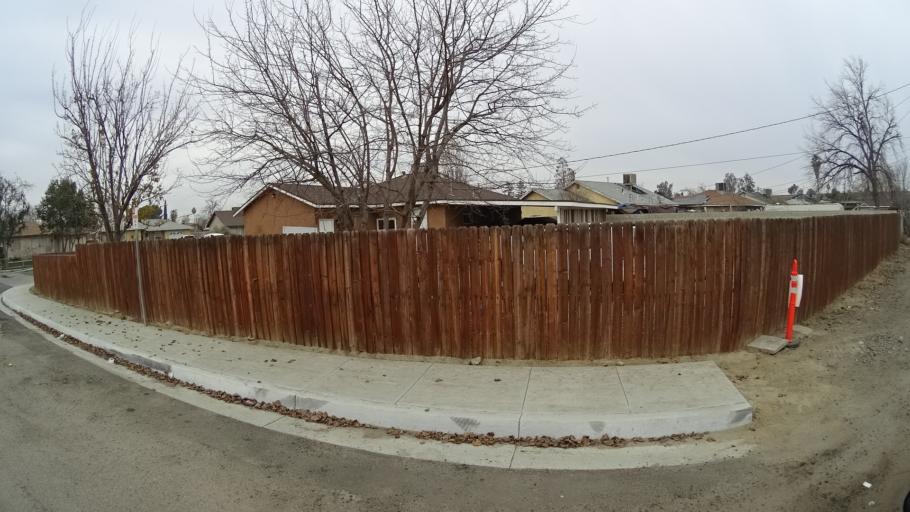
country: US
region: California
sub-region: Kern County
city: Bakersfield
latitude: 35.3502
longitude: -118.9924
